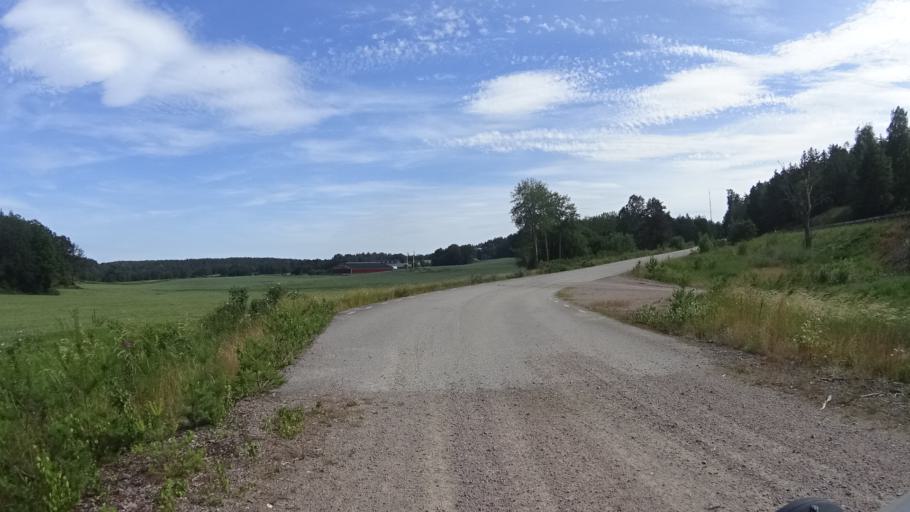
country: SE
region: Kalmar
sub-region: Vasterviks Kommun
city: Gamleby
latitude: 57.9196
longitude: 16.4003
